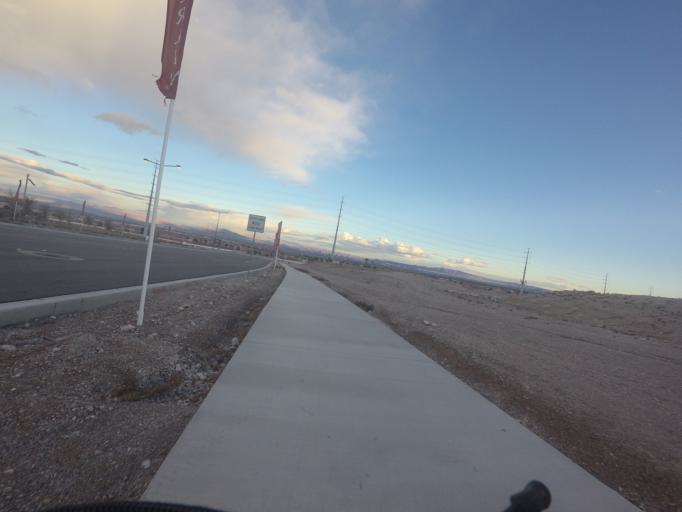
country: US
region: Nevada
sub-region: Clark County
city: Summerlin South
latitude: 36.2060
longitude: -115.3433
